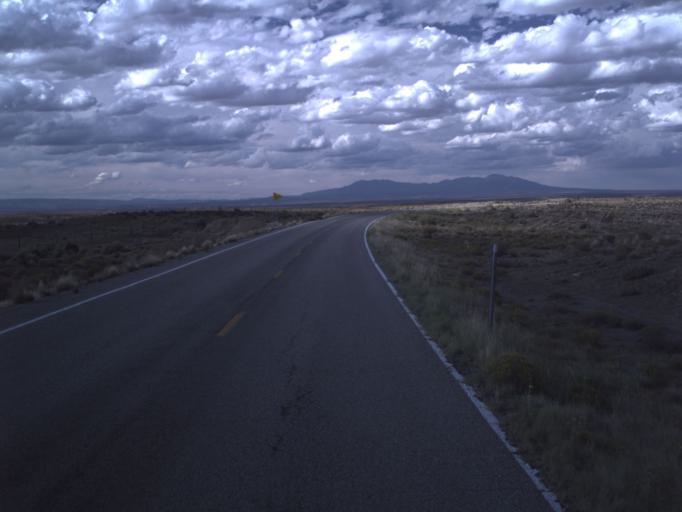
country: US
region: Utah
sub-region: San Juan County
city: Blanding
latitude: 37.3371
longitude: -109.3484
